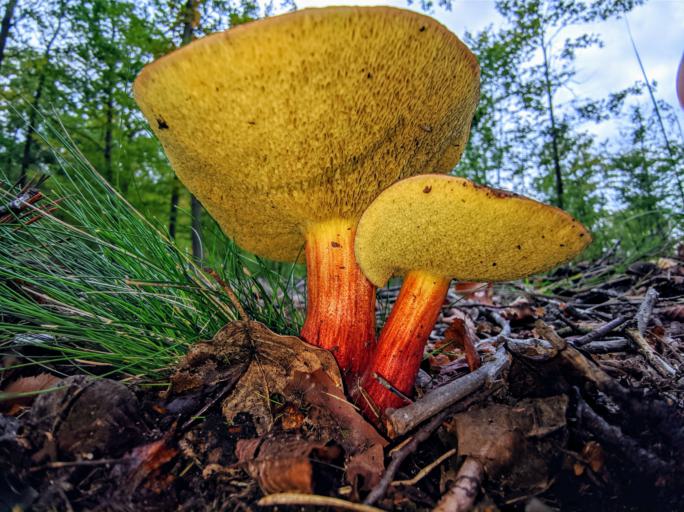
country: PL
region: Lubusz
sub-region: Powiat nowosolski
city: Przyborow
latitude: 51.8324
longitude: 15.7707
